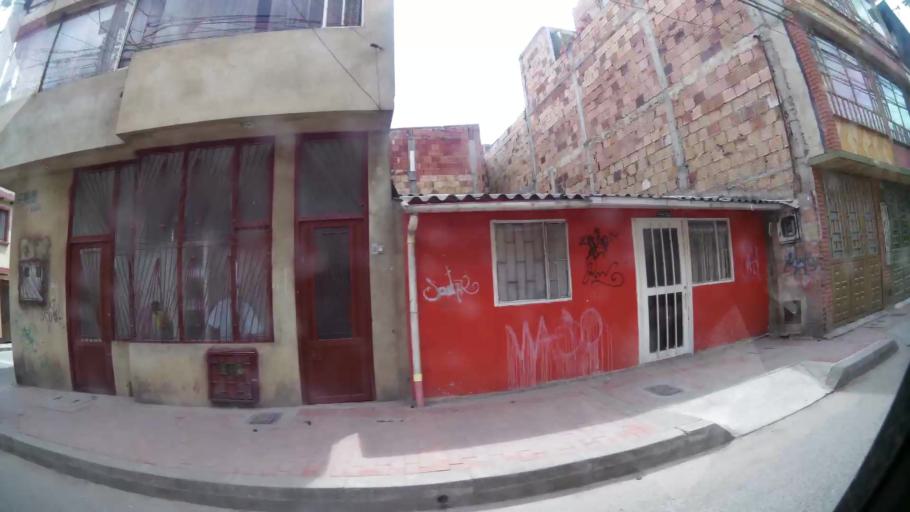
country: CO
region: Cundinamarca
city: Funza
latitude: 4.7144
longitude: -74.1371
